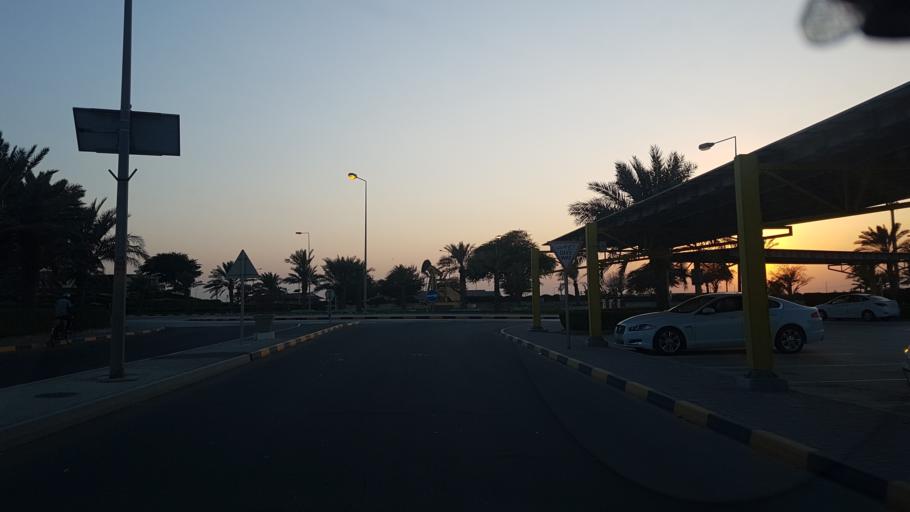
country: BH
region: Northern
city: Ar Rifa'
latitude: 26.0876
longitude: 50.5499
